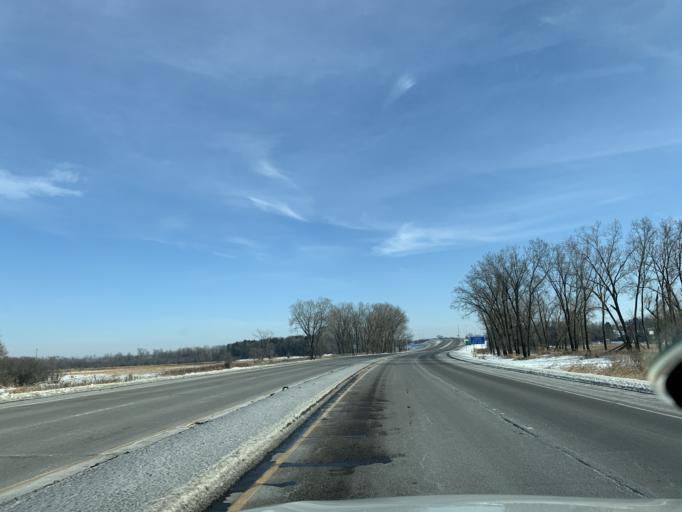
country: US
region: Minnesota
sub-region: Washington County
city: Forest Lake
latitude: 45.2897
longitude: -92.9952
